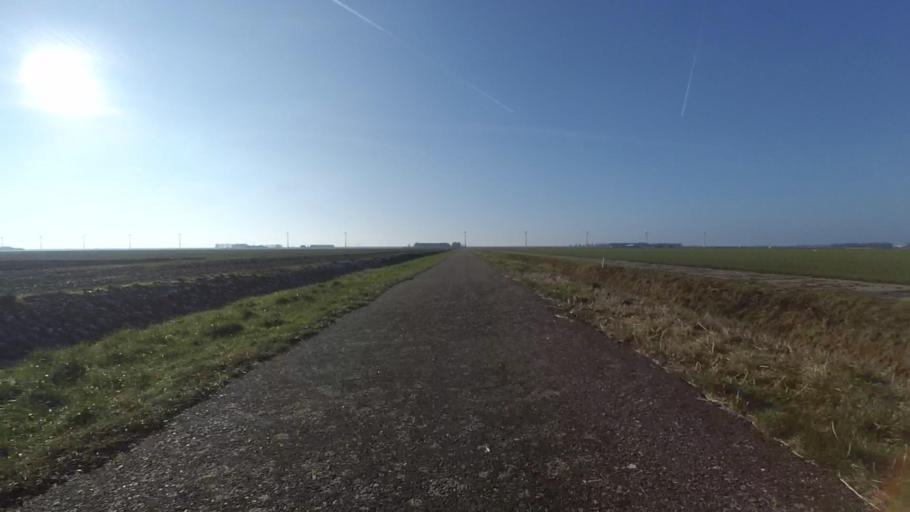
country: NL
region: Utrecht
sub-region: Gemeente Bunschoten
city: Spakenburg
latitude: 52.3021
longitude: 5.3562
